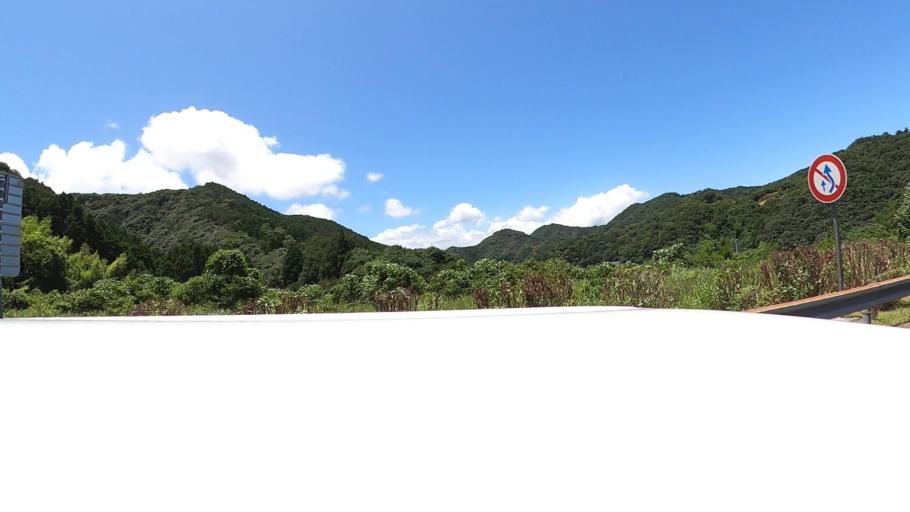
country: JP
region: Miyazaki
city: Nobeoka
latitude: 32.5215
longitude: 131.6649
